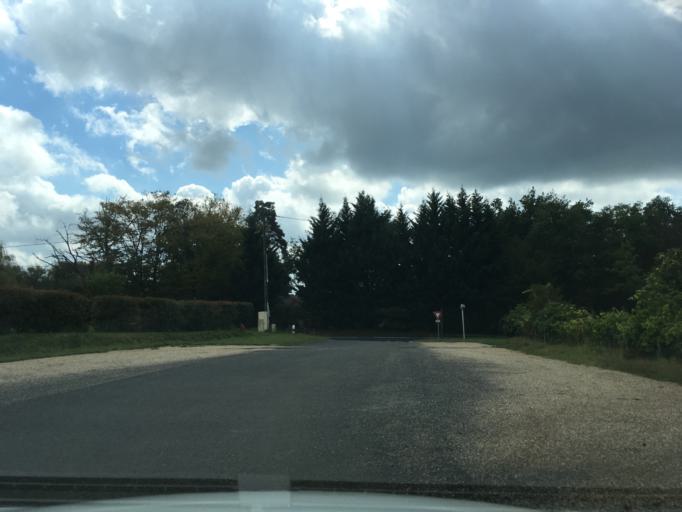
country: FR
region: Limousin
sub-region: Departement de la Correze
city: Brive-la-Gaillarde
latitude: 45.1057
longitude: 1.5461
